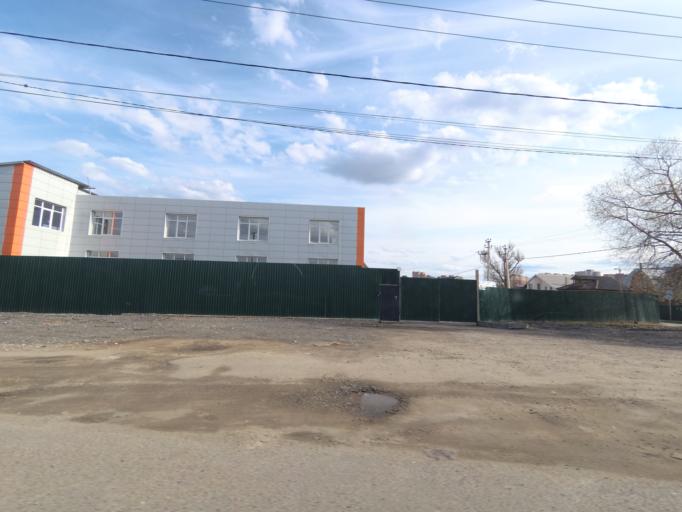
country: RU
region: Moskovskaya
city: Lobnya
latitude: 56.0245
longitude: 37.4320
